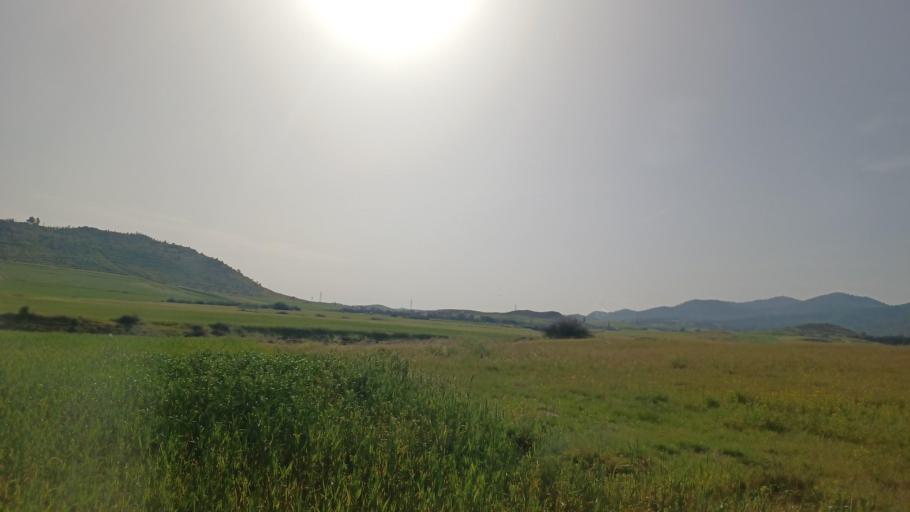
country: CY
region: Lefkosia
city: Lefka
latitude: 35.0911
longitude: 32.9443
